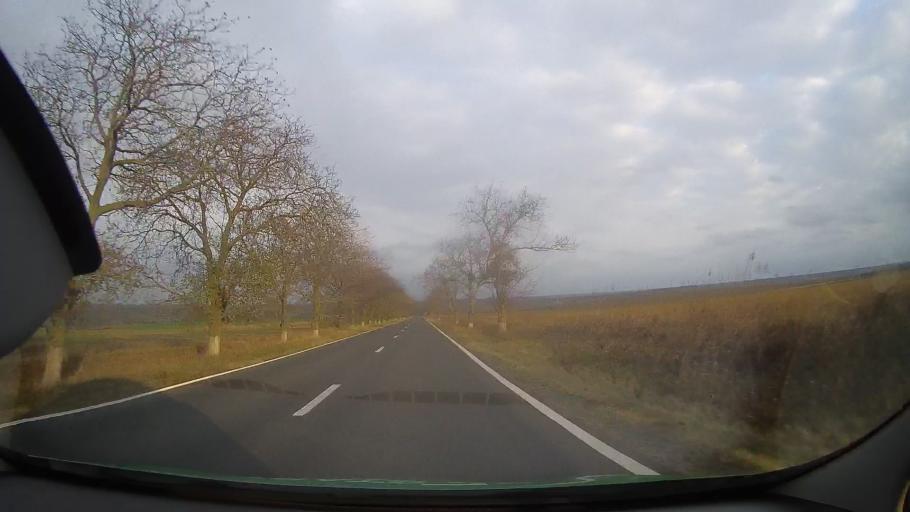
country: RO
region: Constanta
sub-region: Comuna Deleni
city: Deleni
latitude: 44.0887
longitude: 27.9907
